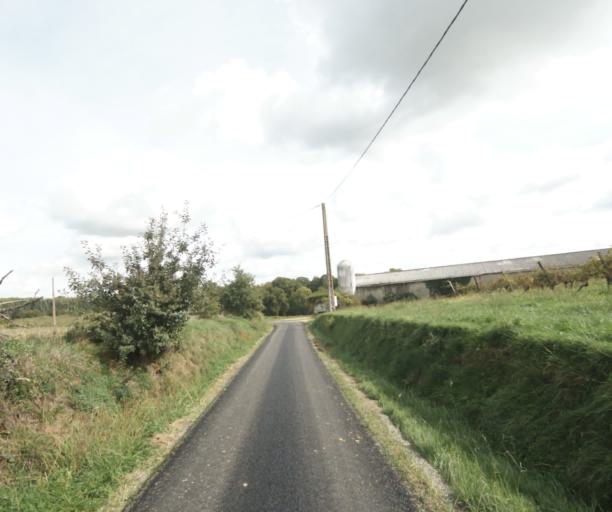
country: FR
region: Midi-Pyrenees
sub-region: Departement du Gers
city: Eauze
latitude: 43.8453
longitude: 0.0746
